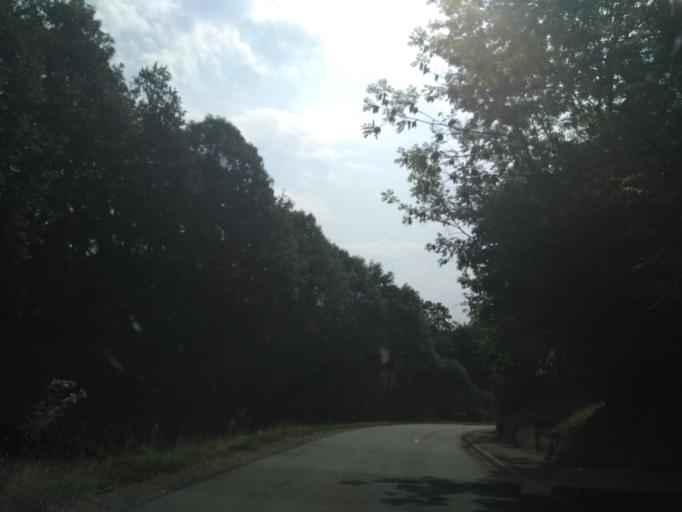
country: DE
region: Thuringia
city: Walpernhain
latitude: 50.9924
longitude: 11.9499
